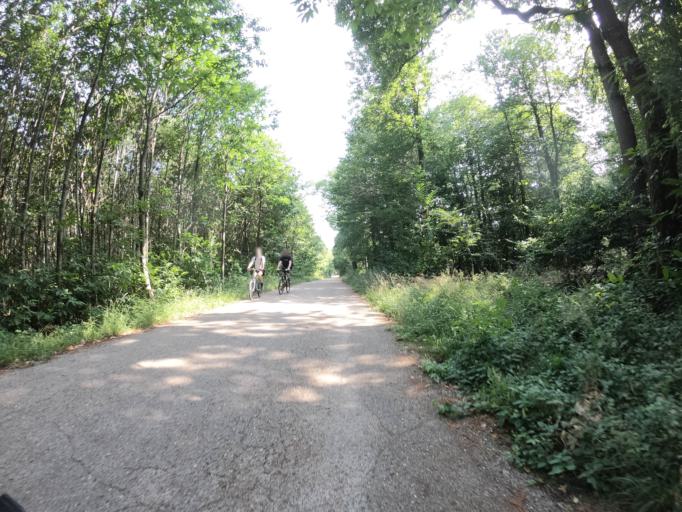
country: FR
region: Ile-de-France
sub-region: Departement de l'Essonne
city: Bievres
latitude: 48.7648
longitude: 2.2366
